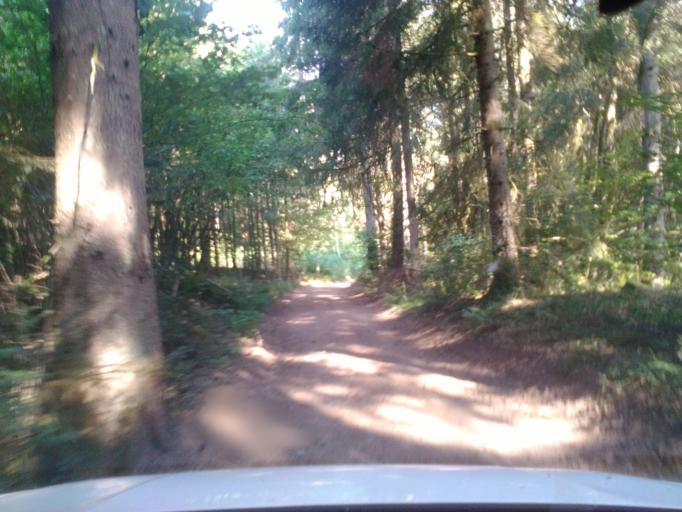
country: FR
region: Lorraine
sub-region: Departement des Vosges
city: Senones
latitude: 48.3615
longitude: 6.9941
